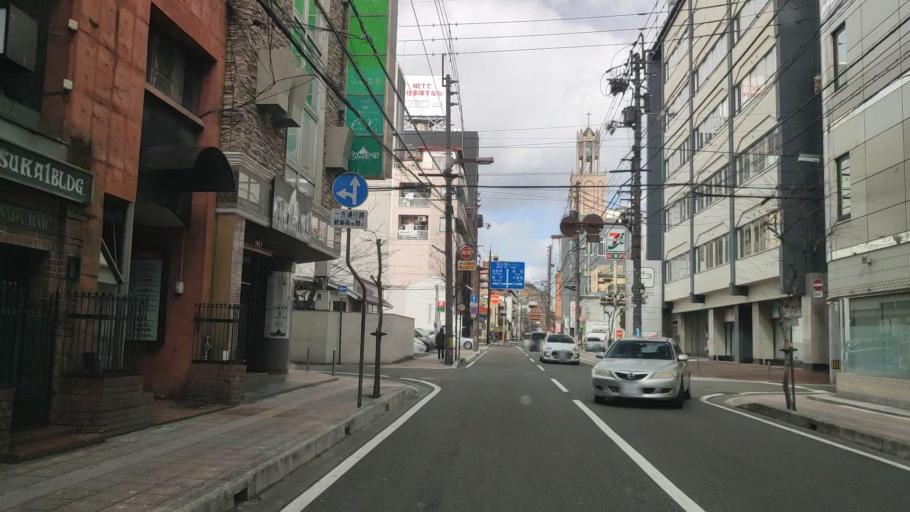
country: JP
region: Ehime
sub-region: Shikoku-chuo Shi
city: Matsuyama
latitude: 33.8403
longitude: 132.7722
